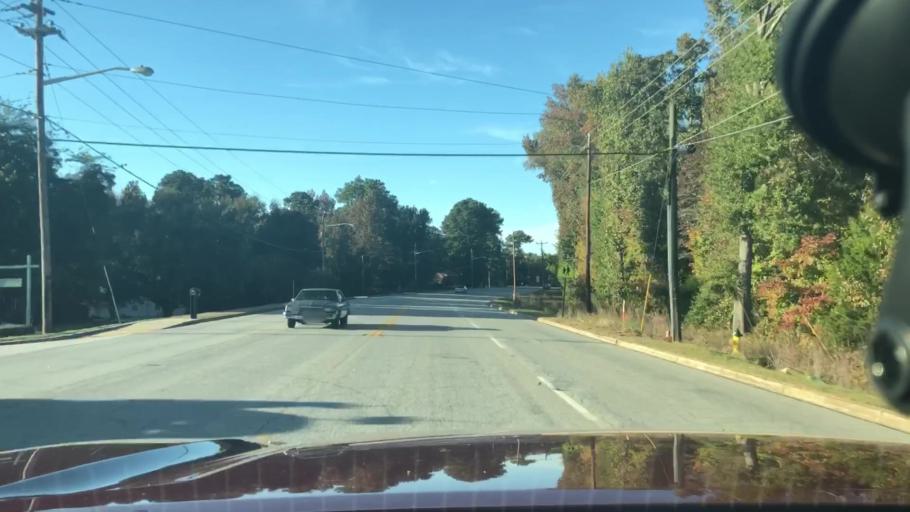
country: US
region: South Carolina
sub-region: Greenwood County
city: Greenwood
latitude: 34.2223
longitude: -82.1406
